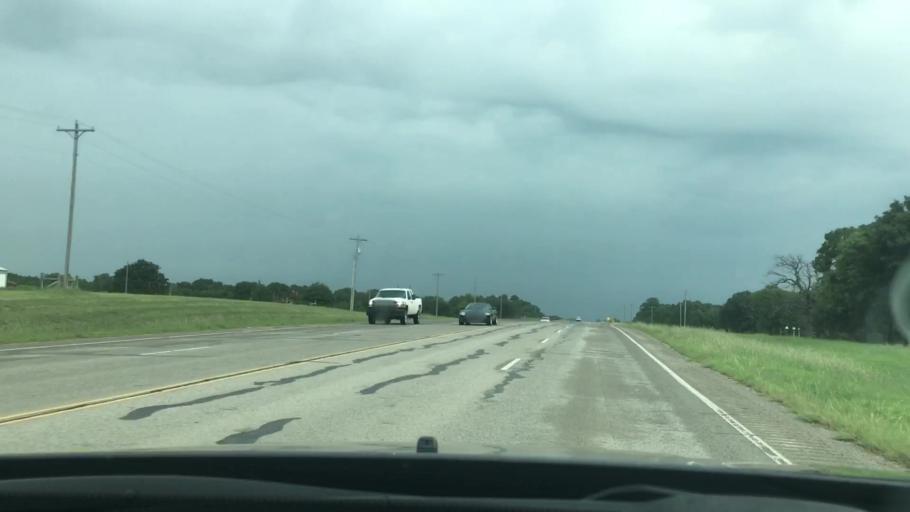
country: US
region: Oklahoma
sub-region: Carter County
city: Healdton
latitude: 34.1920
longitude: -97.4747
